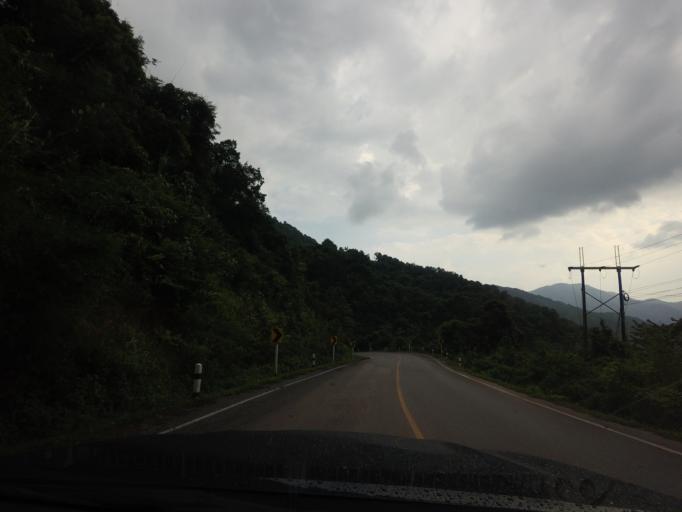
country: TH
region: Nan
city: Bo Kluea
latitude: 19.1617
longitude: 101.1400
